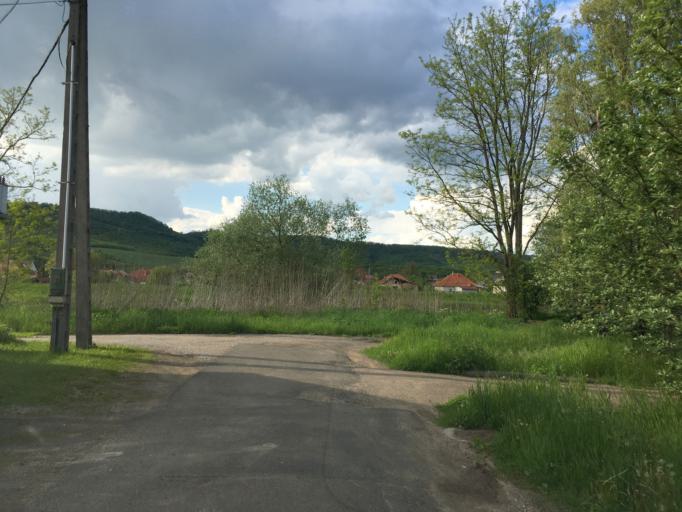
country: HU
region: Nograd
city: Matraverebely
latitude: 47.9700
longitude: 19.7741
